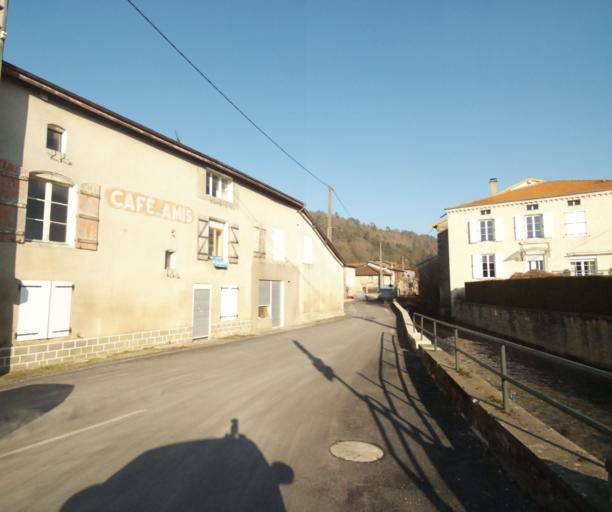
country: FR
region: Champagne-Ardenne
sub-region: Departement de la Haute-Marne
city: Chevillon
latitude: 48.4918
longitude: 5.1360
